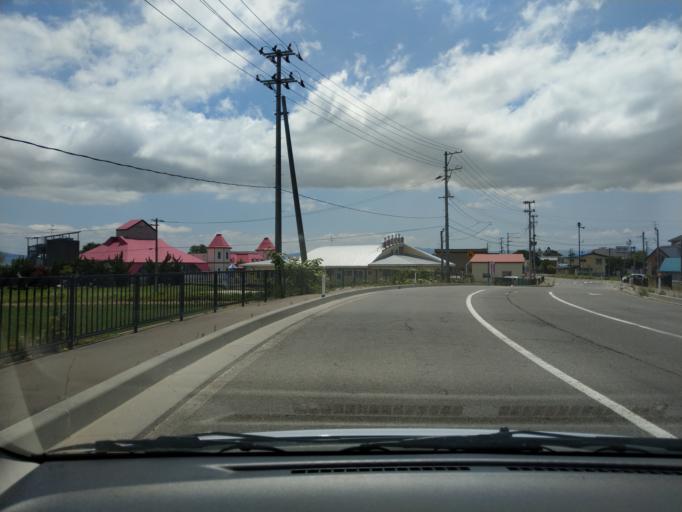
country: JP
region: Aomori
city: Namioka
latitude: 40.6906
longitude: 140.5588
